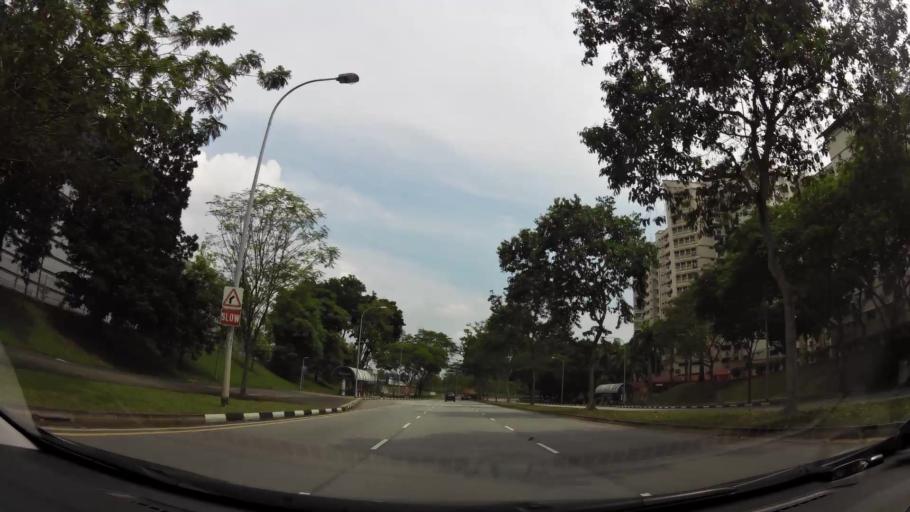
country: MY
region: Johor
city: Kampung Pasir Gudang Baru
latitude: 1.3824
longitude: 103.9356
